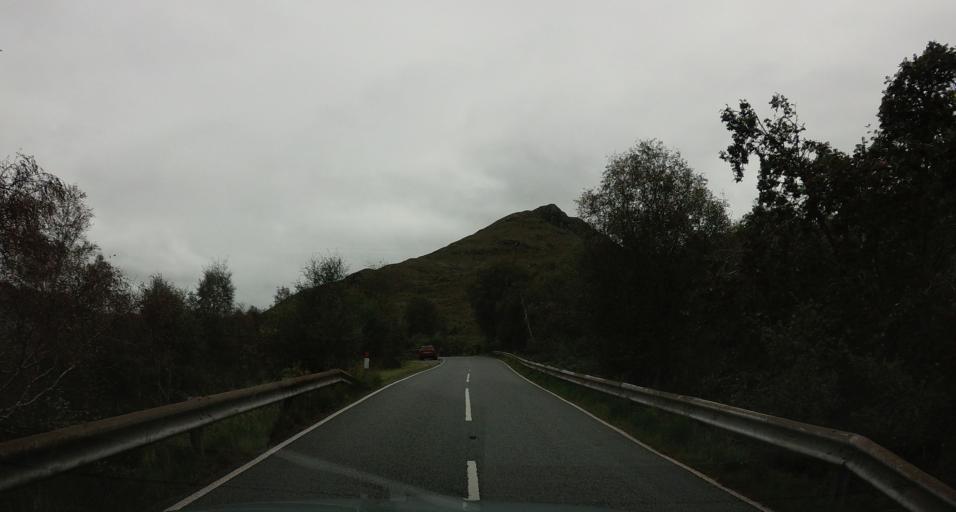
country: GB
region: Scotland
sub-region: Highland
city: Fort William
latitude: 56.7015
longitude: -5.0368
